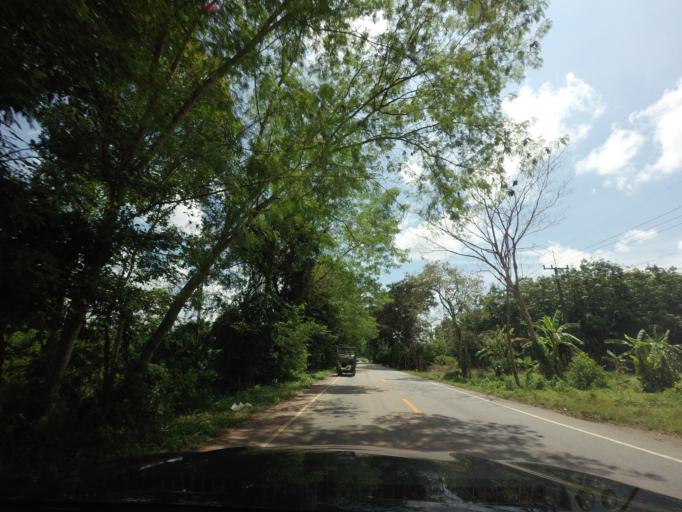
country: TH
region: Nong Khai
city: Pho Tak
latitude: 17.7845
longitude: 102.3730
